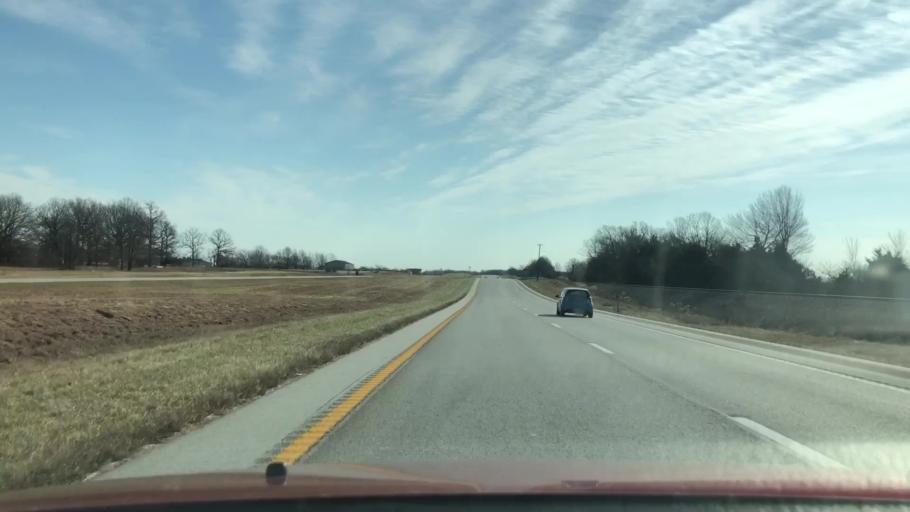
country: US
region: Missouri
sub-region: Webster County
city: Seymour
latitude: 37.1653
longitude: -92.8017
